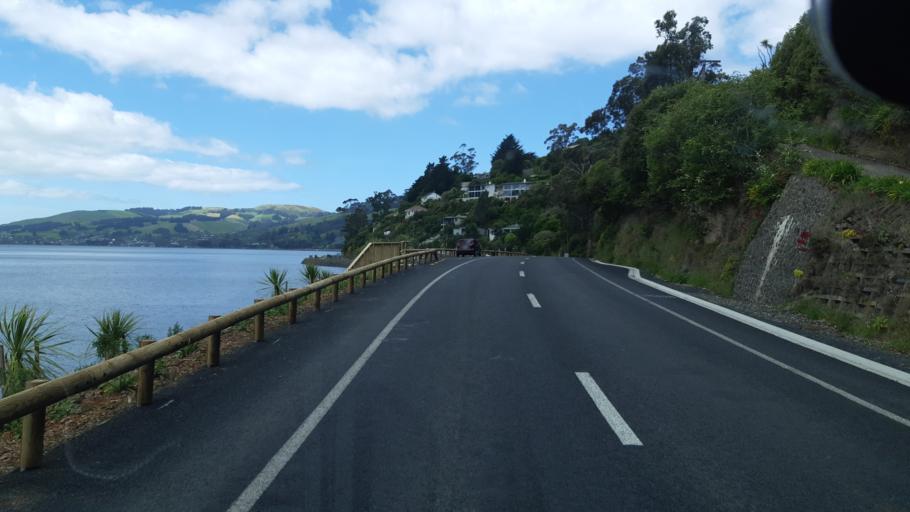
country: NZ
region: Otago
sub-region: Dunedin City
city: Dunedin
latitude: -45.8797
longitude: 170.5467
